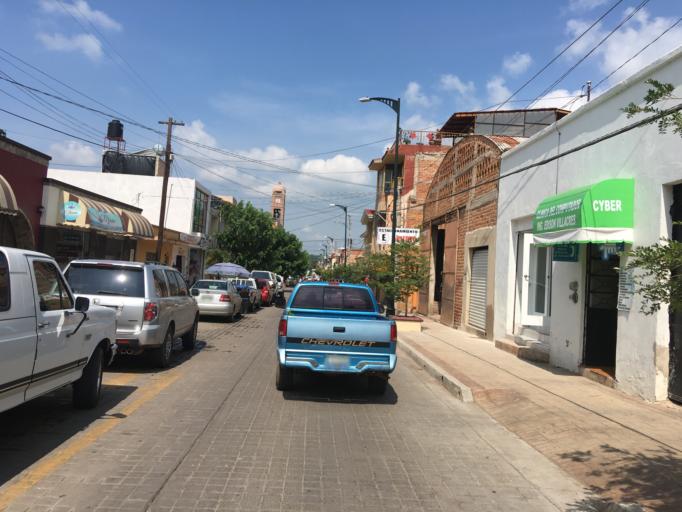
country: MX
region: Jalisco
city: Atotonilco el Alto
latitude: 20.5489
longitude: -102.5114
